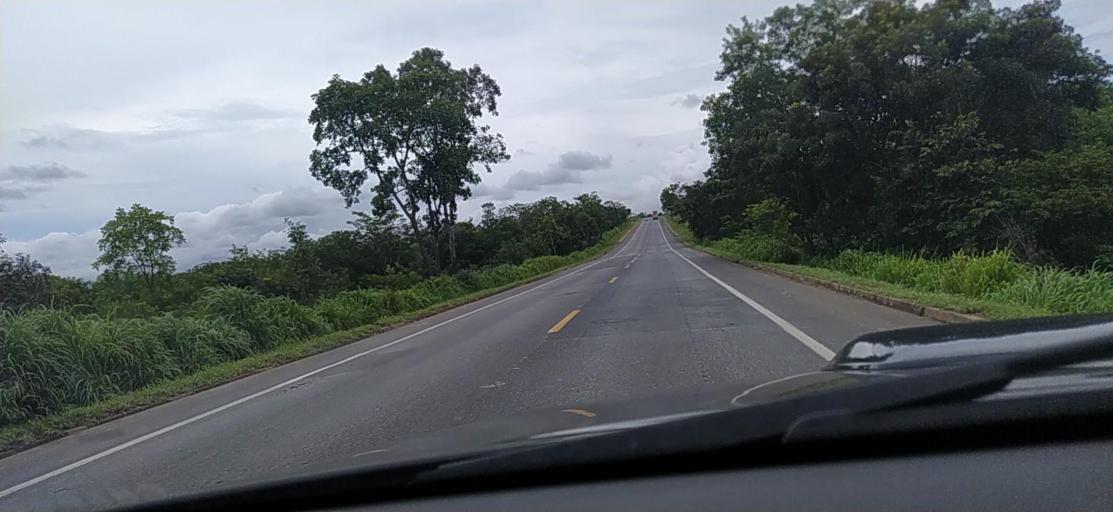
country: BR
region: Minas Gerais
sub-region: Corinto
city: Corinto
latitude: -18.3037
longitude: -44.4134
